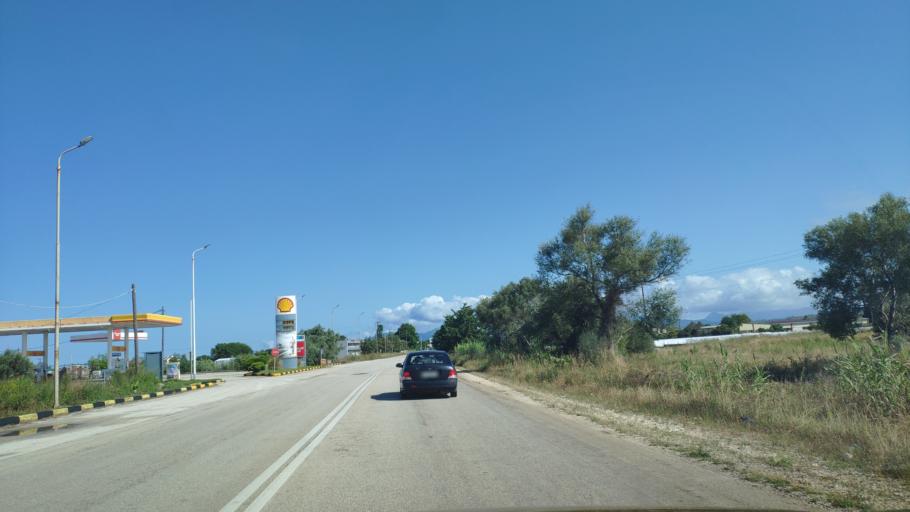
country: GR
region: Epirus
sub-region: Nomos Prevezis
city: Preveza
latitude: 38.9805
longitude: 20.7166
